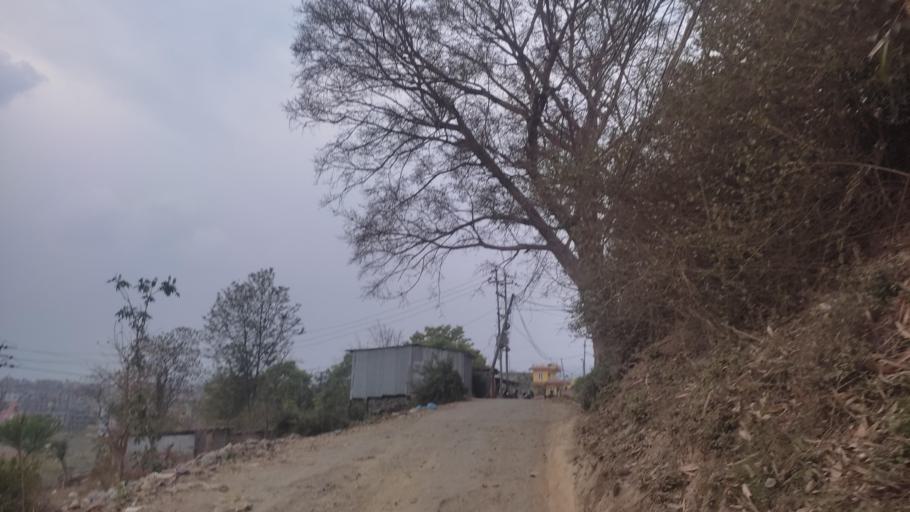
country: NP
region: Central Region
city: Kirtipur
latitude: 27.6650
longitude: 85.2865
